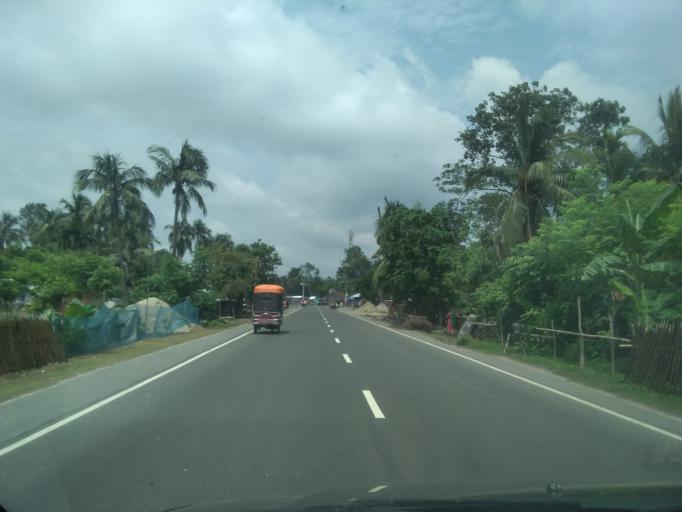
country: BD
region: Khulna
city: Kesabpur
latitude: 22.7808
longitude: 89.2056
